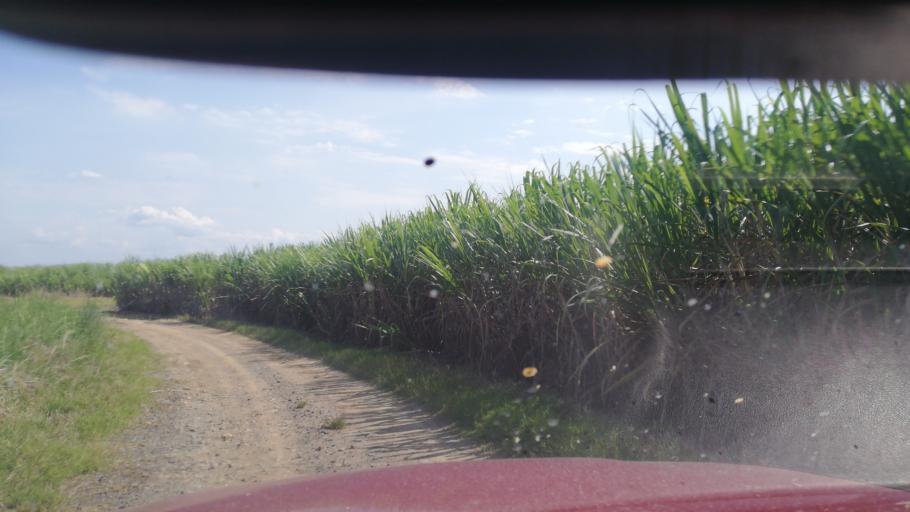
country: CO
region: Risaralda
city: La Virginia
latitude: 4.8934
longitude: -75.9280
